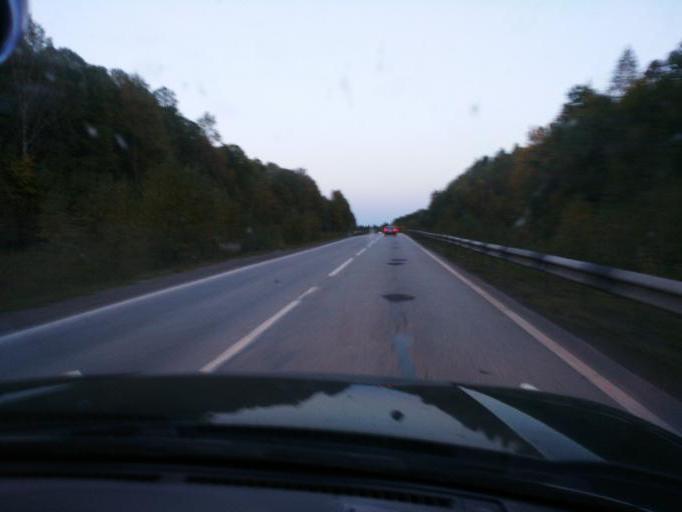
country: RU
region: Perm
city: Verkhnechusovskiye Gorodki
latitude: 58.2668
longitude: 56.9592
